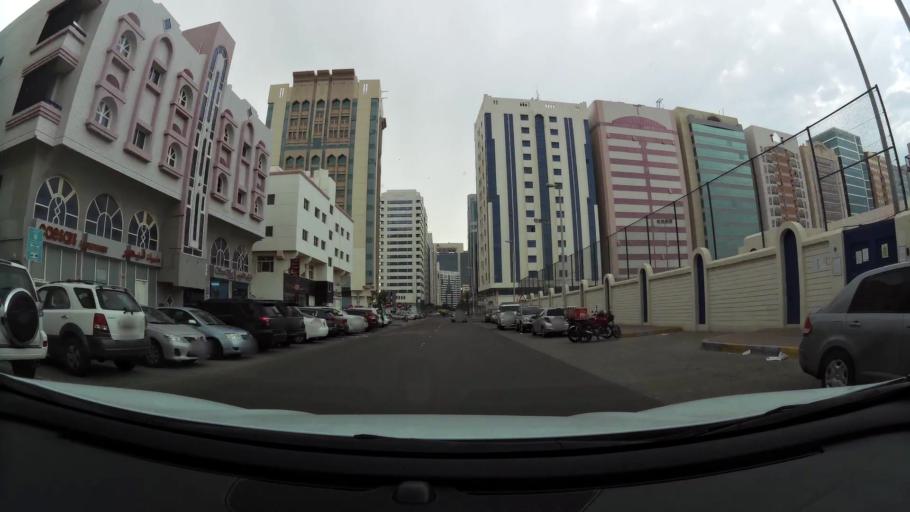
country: AE
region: Abu Dhabi
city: Abu Dhabi
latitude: 24.4751
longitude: 54.3761
